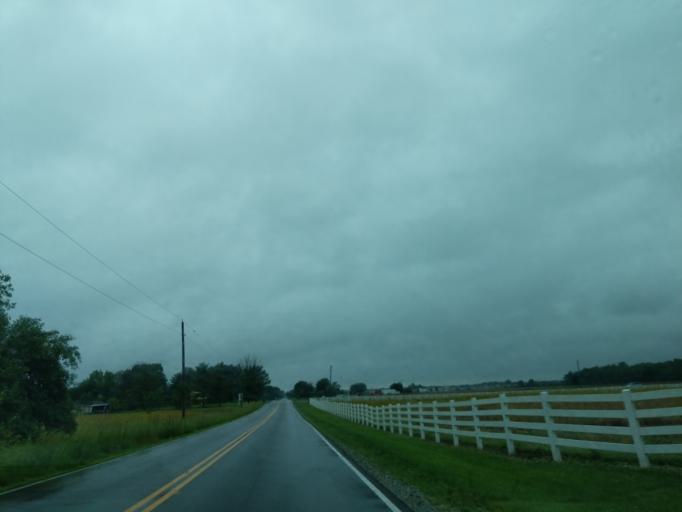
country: US
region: Indiana
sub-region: Hamilton County
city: Noblesville
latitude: 40.0661
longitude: -85.9559
